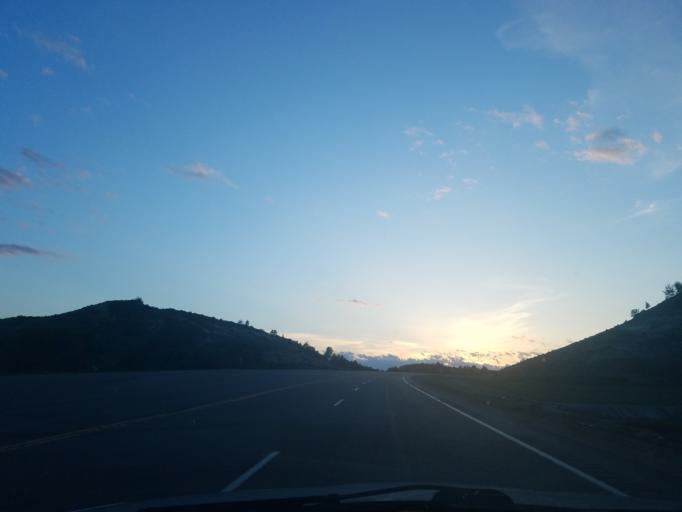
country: US
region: North Dakota
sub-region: McKenzie County
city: Watford City
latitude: 47.6105
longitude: -103.2625
